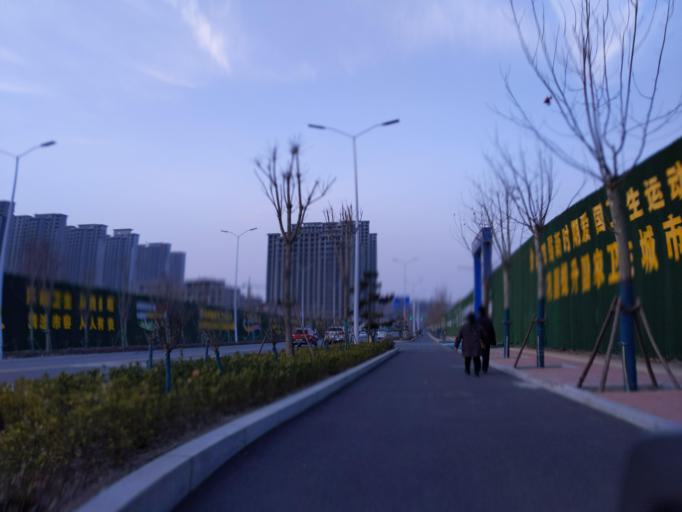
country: CN
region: Henan Sheng
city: Puyang
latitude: 35.8116
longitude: 115.0115
